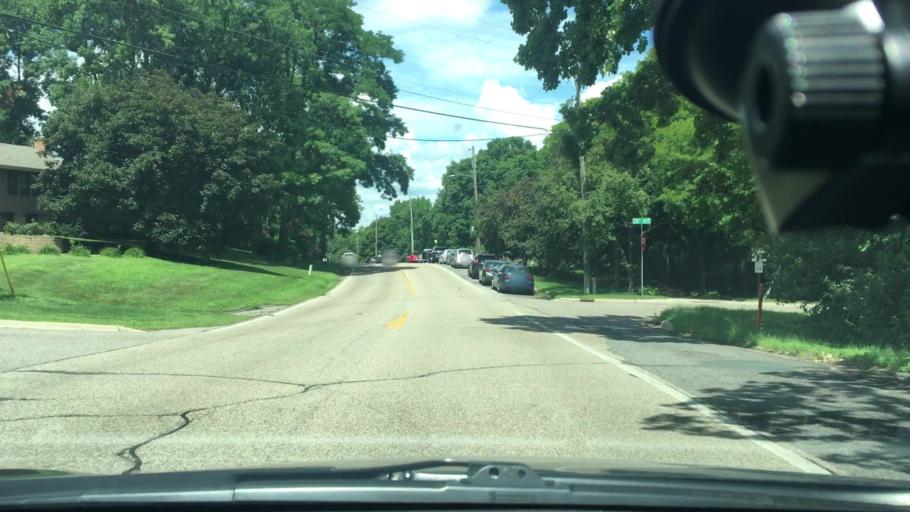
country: US
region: Minnesota
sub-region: Hennepin County
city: Plymouth
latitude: 45.0099
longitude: -93.4342
